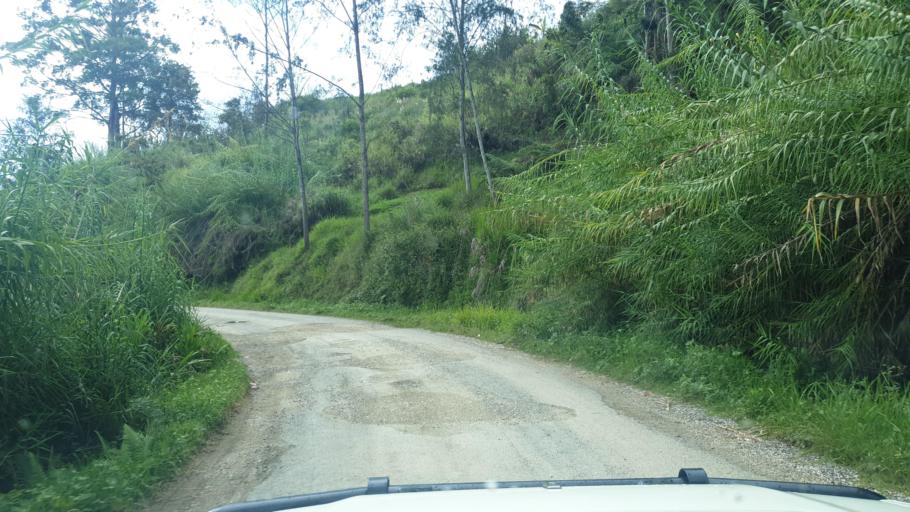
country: PG
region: Chimbu
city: Kundiawa
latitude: -6.1633
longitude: 145.1338
